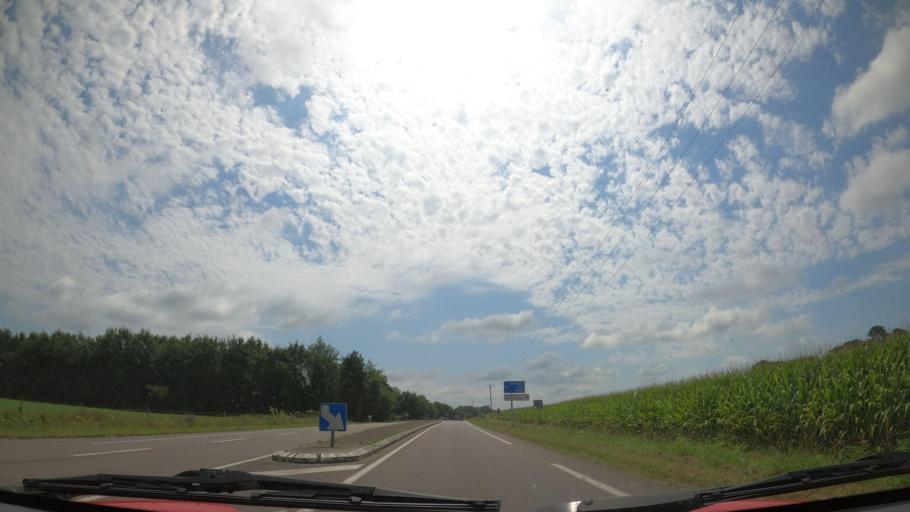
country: FR
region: Aquitaine
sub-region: Departement des Landes
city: Peyrehorade
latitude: 43.5206
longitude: -1.1060
